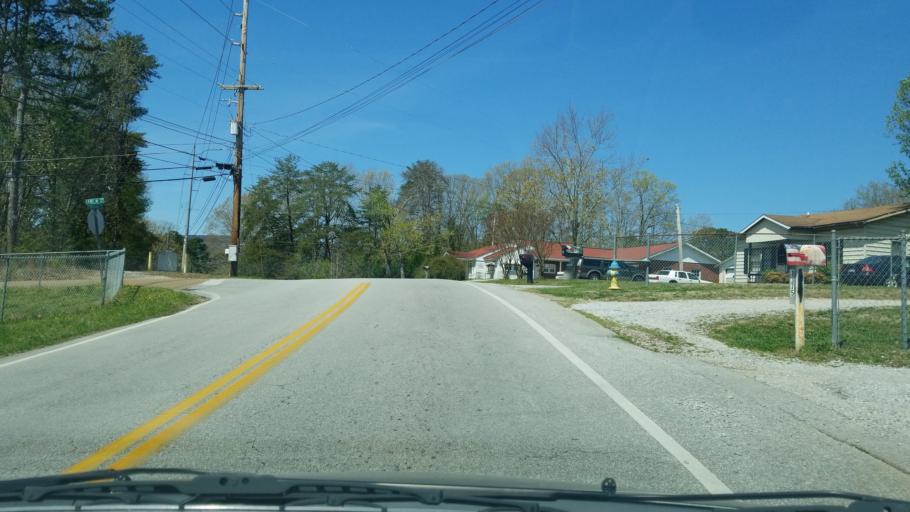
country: US
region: Tennessee
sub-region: Hamilton County
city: Middle Valley
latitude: 35.1979
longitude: -85.2000
